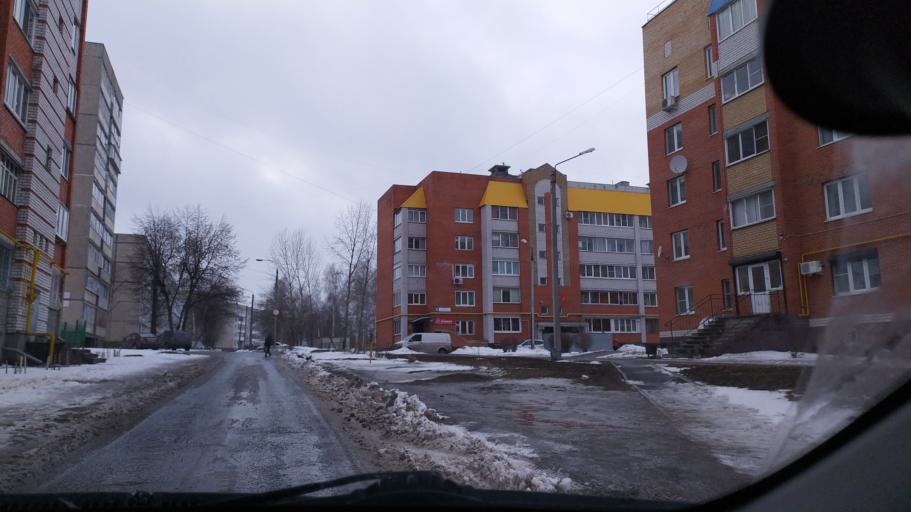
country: RU
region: Chuvashia
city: Novocheboksarsk
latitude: 56.1254
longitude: 47.4915
